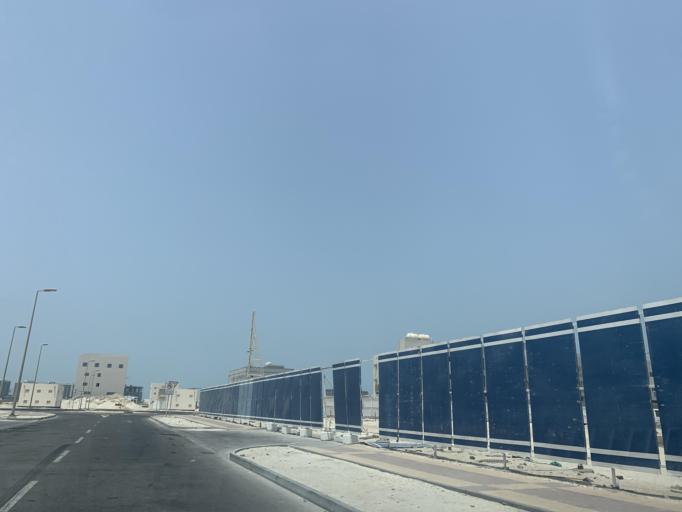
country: BH
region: Muharraq
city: Al Hadd
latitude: 26.2591
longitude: 50.6691
